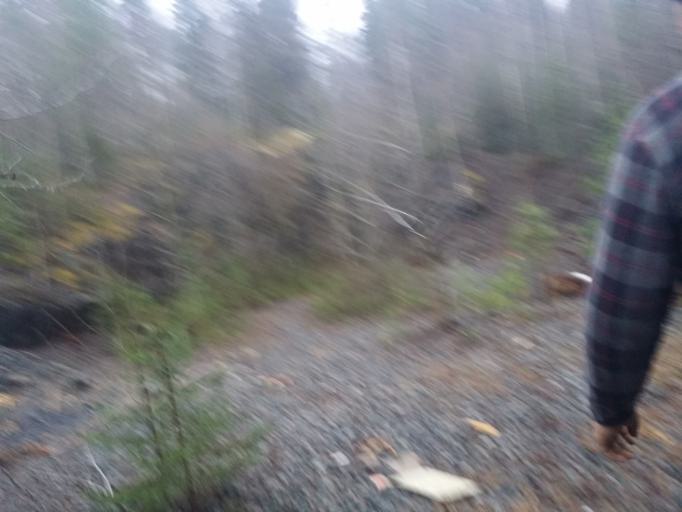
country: SE
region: Vaestmanland
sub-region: Norbergs Kommun
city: Norberg
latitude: 60.1228
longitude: 16.0334
